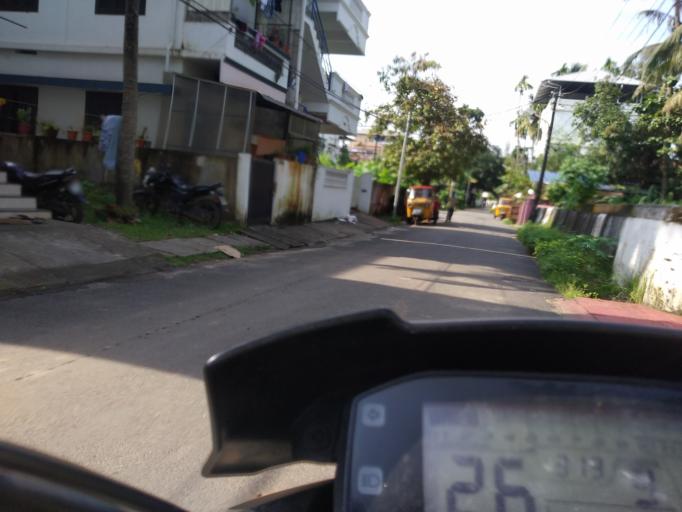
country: IN
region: Kerala
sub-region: Ernakulam
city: Cochin
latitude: 9.9810
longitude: 76.2937
